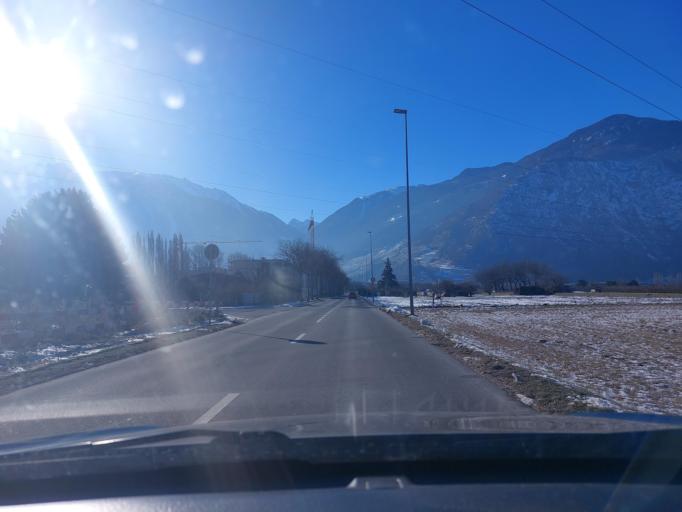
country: CH
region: Valais
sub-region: Martigny District
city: Martigny-Ville
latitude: 46.1127
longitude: 7.0883
